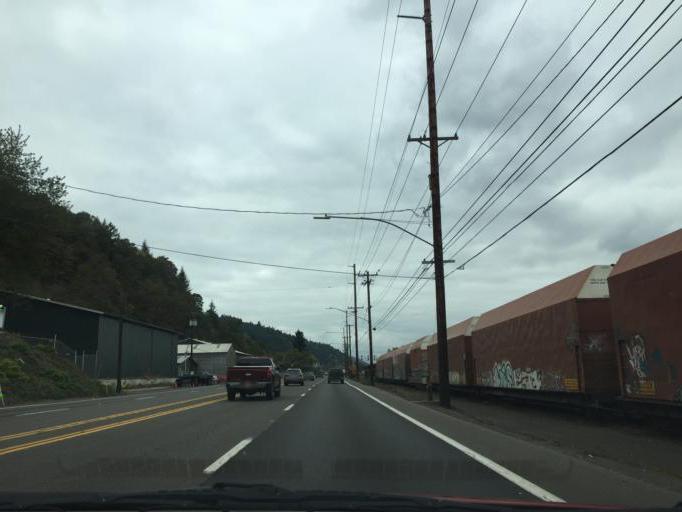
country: US
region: Oregon
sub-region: Washington County
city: West Haven
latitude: 45.5590
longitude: -122.7398
